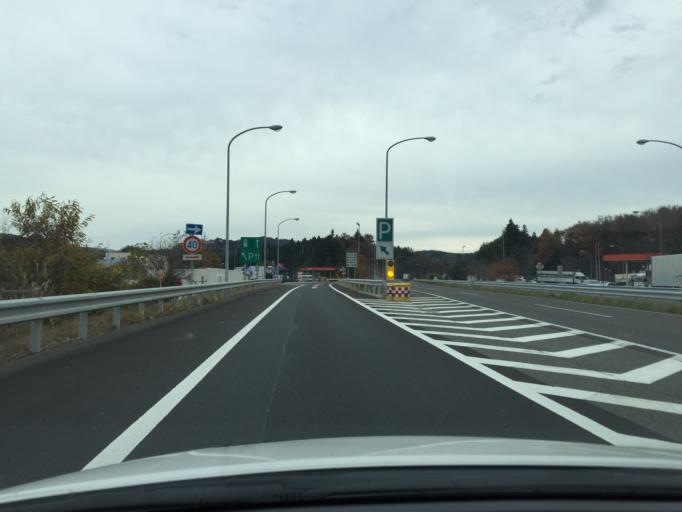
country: JP
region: Fukushima
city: Funehikimachi-funehiki
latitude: 37.3888
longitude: 140.5941
